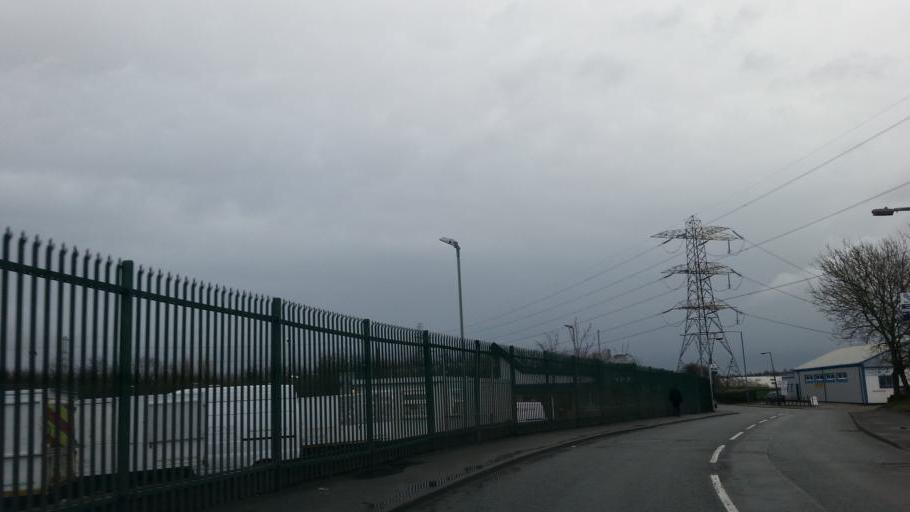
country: GB
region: England
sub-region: Sandwell
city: Oldbury
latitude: 52.4997
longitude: -2.0265
